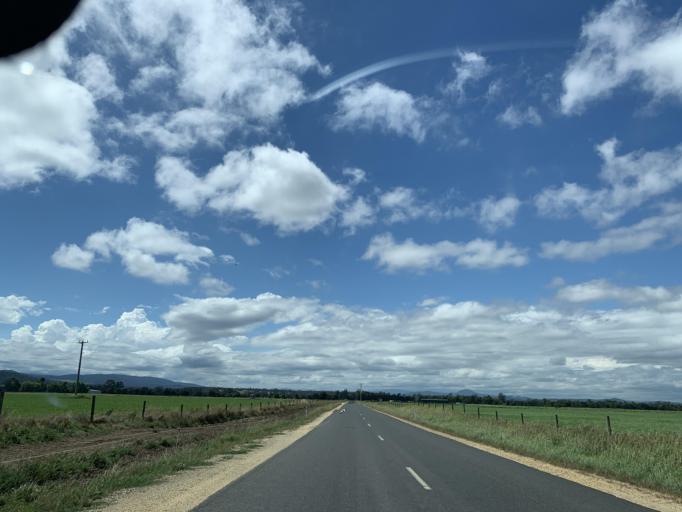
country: AU
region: Victoria
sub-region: Wellington
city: Heyfield
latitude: -37.9981
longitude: 146.6917
